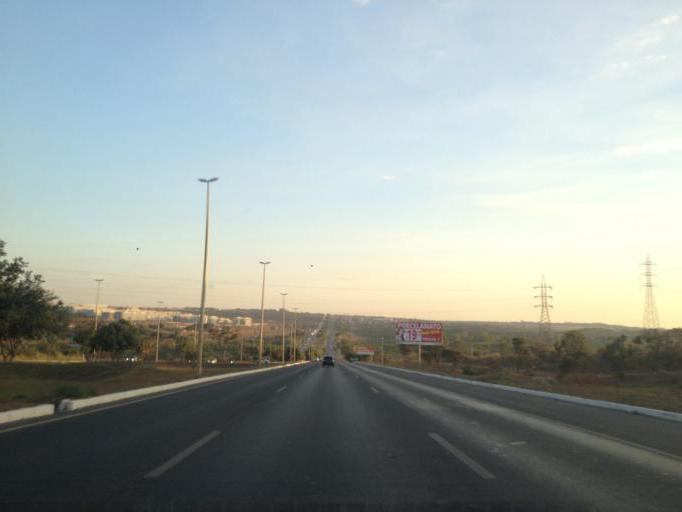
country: BR
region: Federal District
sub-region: Brasilia
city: Brasilia
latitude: -15.7201
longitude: -47.9047
